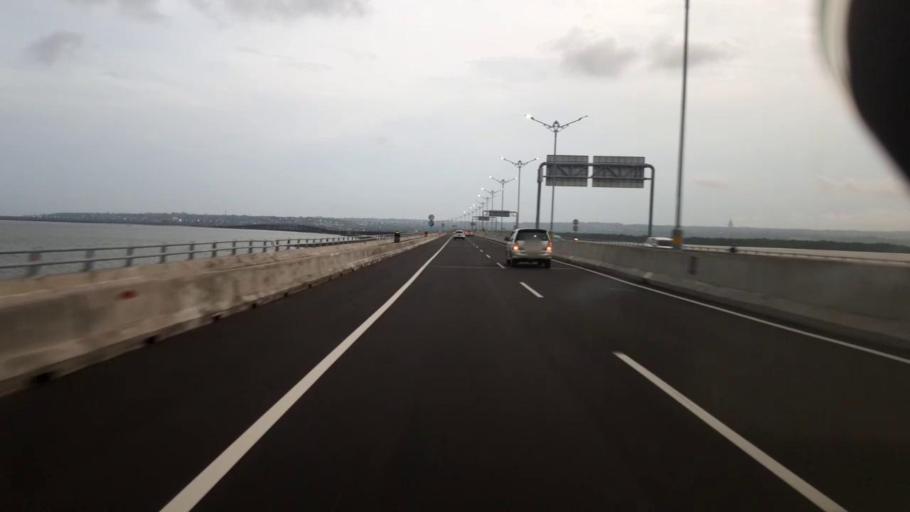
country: ID
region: Bali
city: Kelanabian
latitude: -8.7543
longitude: 115.1953
